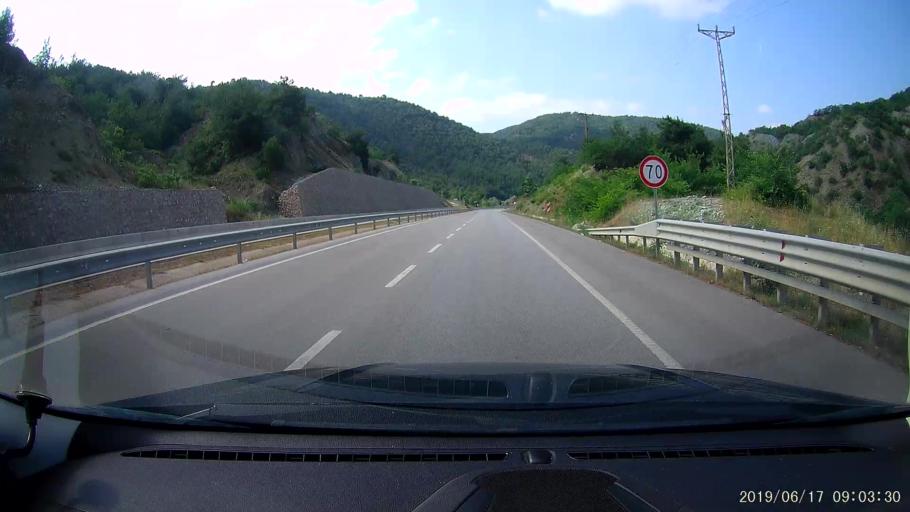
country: TR
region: Amasya
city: Tasova
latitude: 40.7547
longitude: 36.3023
